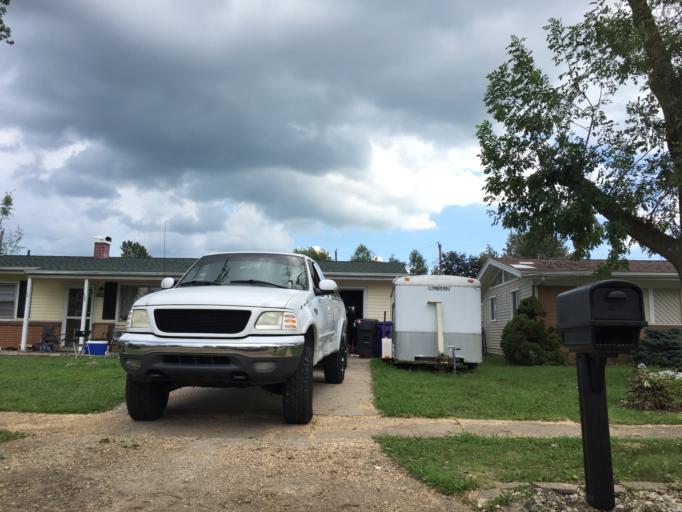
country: US
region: Indiana
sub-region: Howard County
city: Kokomo
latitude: 40.4685
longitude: -86.1065
